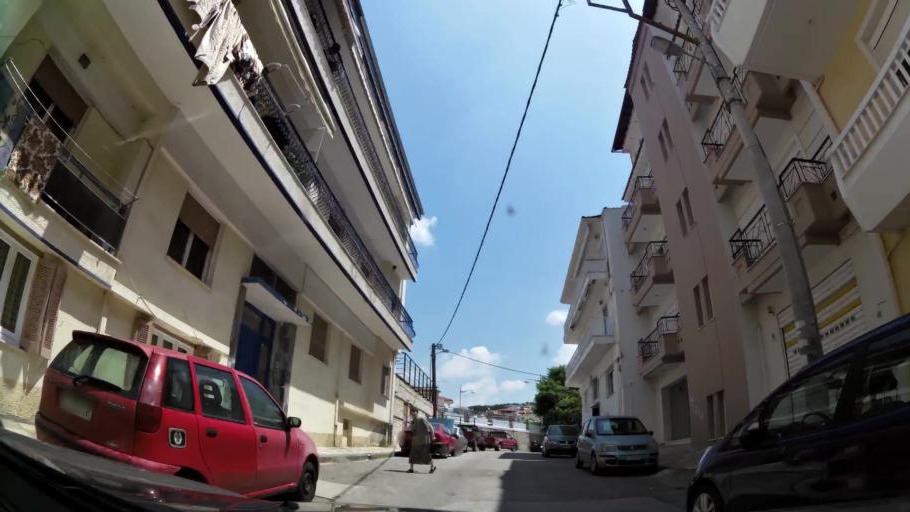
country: GR
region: West Macedonia
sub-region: Nomos Kozanis
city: Kozani
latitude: 40.3056
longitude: 21.7885
